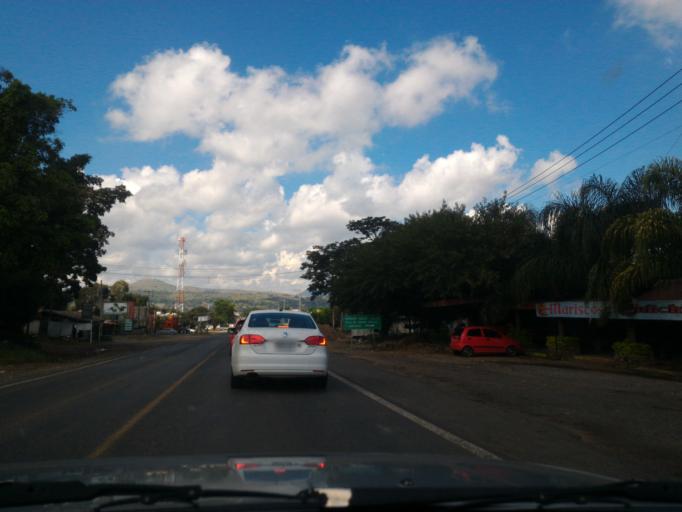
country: MX
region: Jalisco
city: Tequila
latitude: 20.8781
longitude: -103.8189
